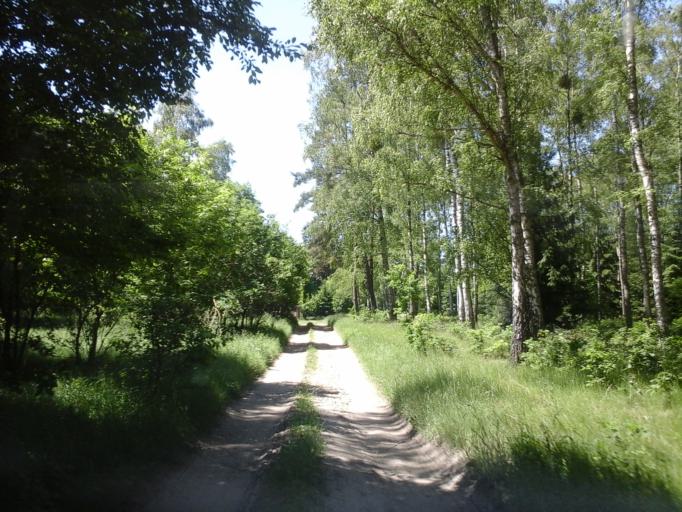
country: PL
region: West Pomeranian Voivodeship
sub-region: Powiat walecki
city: Czlopa
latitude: 53.1223
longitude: 15.9588
